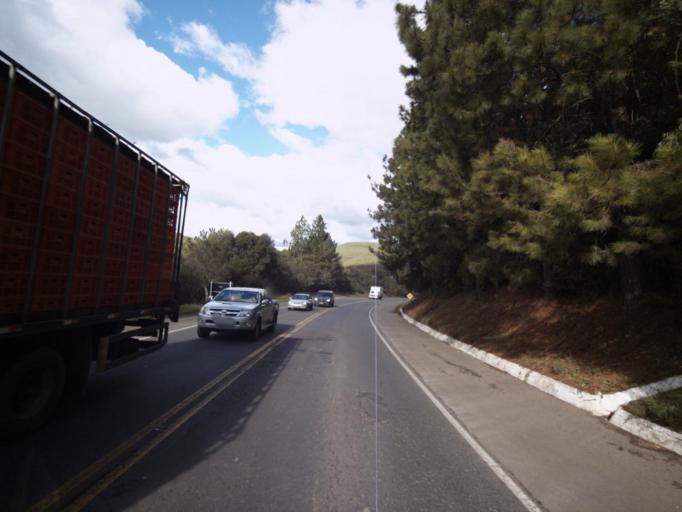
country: BR
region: Santa Catarina
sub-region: Joacaba
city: Joacaba
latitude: -27.0498
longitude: -51.7012
